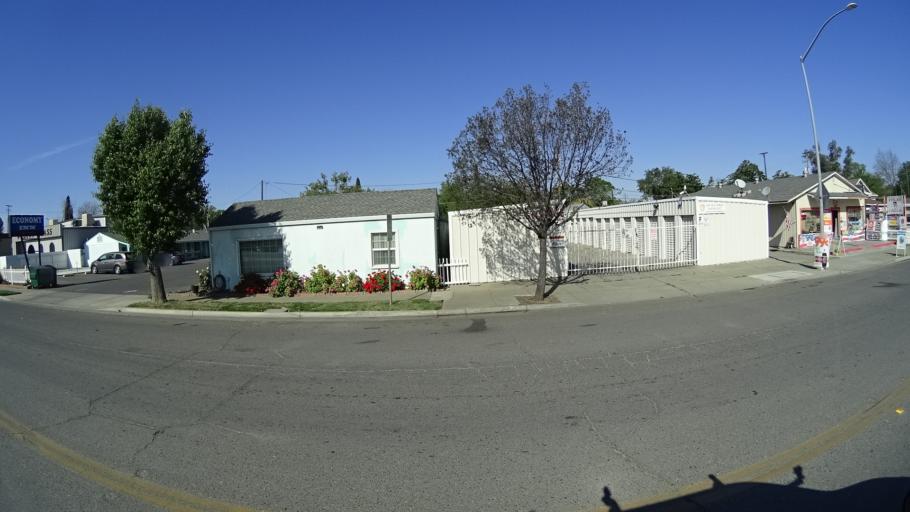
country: US
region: California
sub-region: Glenn County
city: Willows
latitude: 39.5248
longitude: -122.1939
